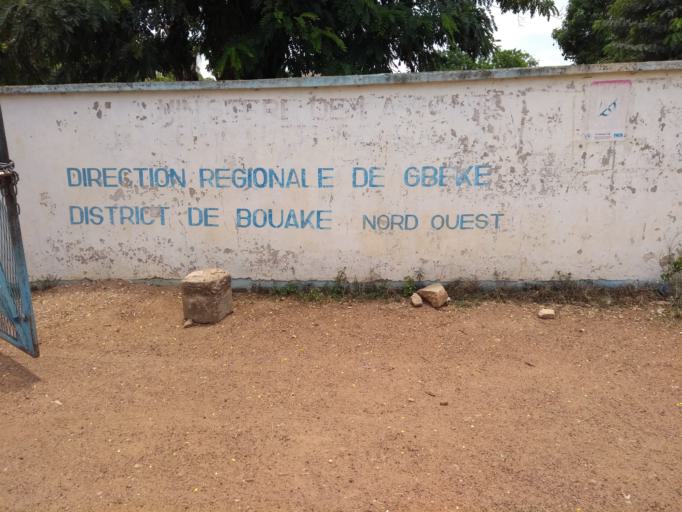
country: CI
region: Vallee du Bandama
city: Bouake
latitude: 7.6763
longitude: -5.0415
